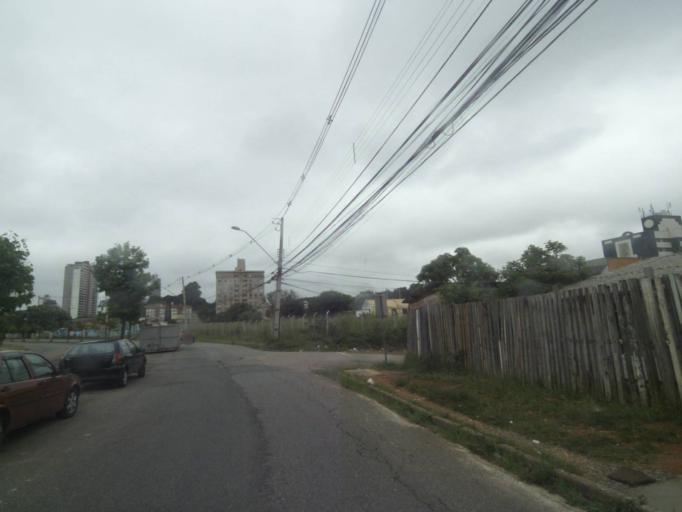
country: BR
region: Parana
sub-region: Curitiba
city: Curitiba
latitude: -25.4394
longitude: -49.3173
